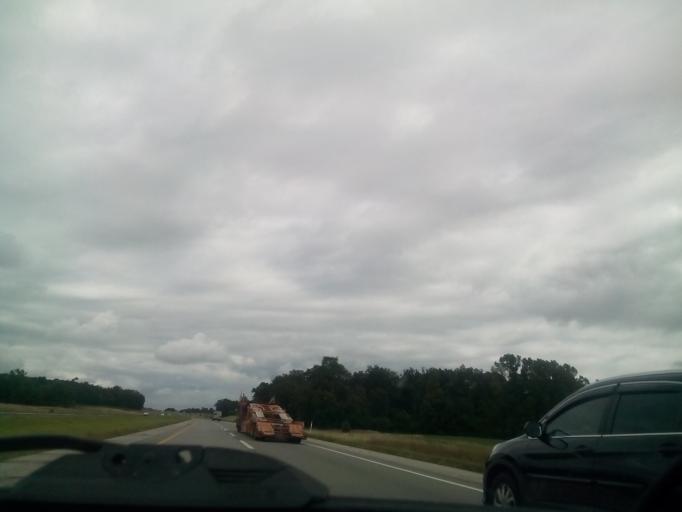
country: US
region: Michigan
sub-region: Saint Joseph County
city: Sturgis
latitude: 41.7420
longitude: -85.3114
